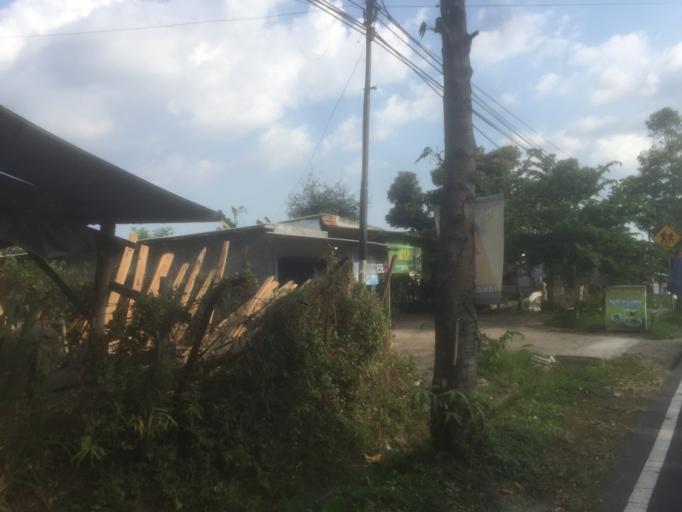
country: ID
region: Daerah Istimewa Yogyakarta
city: Sleman
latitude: -7.6576
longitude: 110.4224
